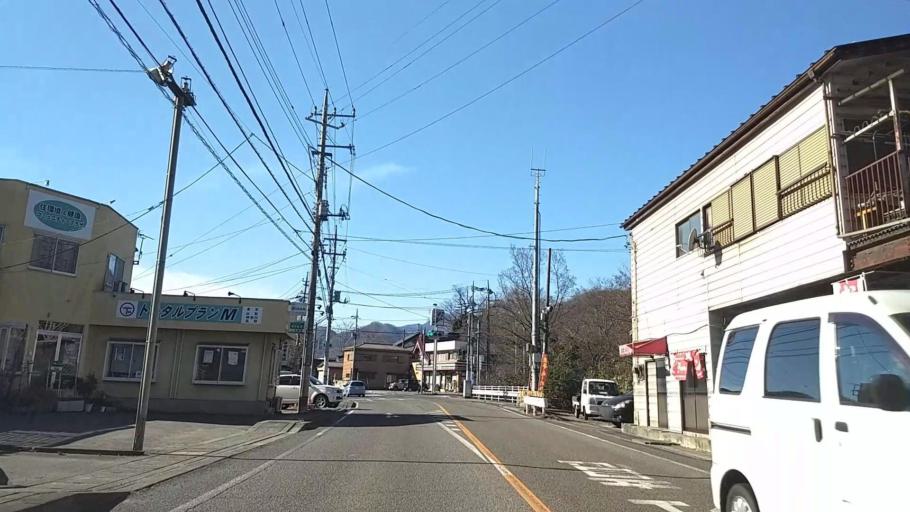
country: JP
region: Yamanashi
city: Otsuki
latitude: 35.6144
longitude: 138.9691
